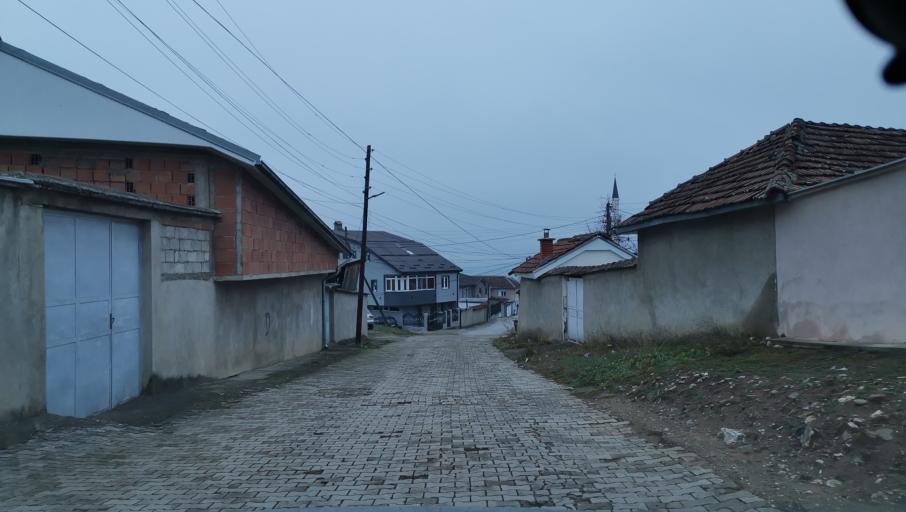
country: MK
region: Debar
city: Debar
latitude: 41.5273
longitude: 20.5254
